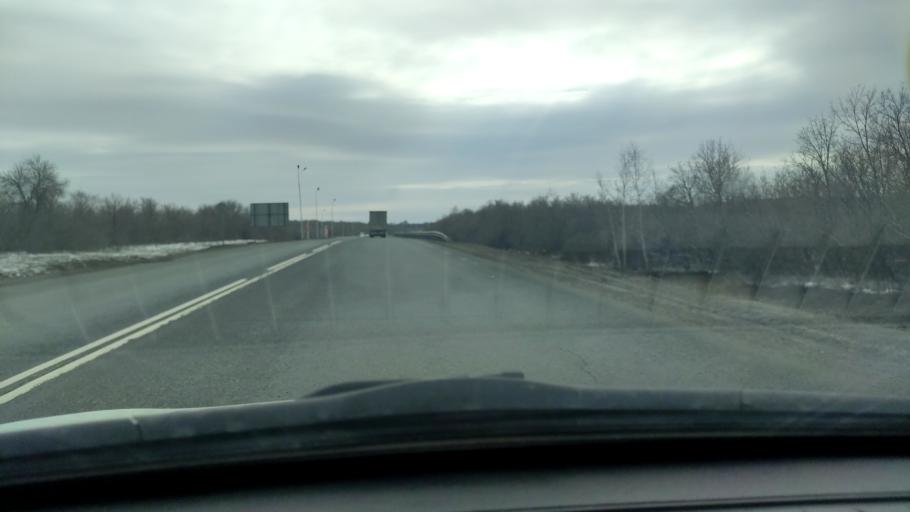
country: RU
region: Samara
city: Zhigulevsk
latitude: 53.3493
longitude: 49.4519
